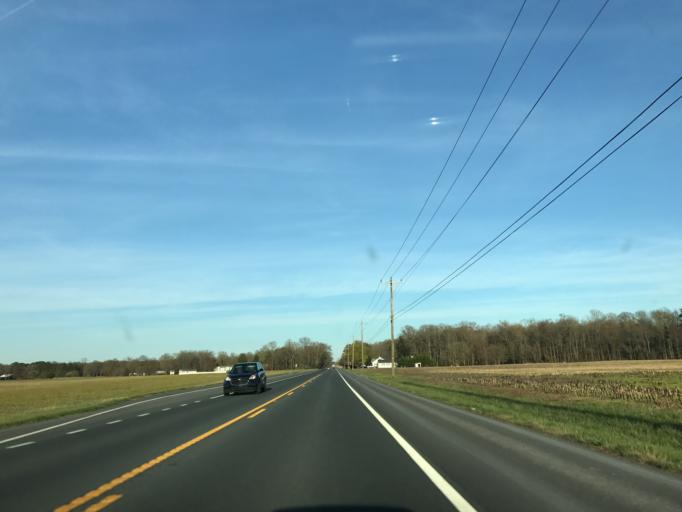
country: US
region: Delaware
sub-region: Kent County
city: Wyoming
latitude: 39.1558
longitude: -75.6112
